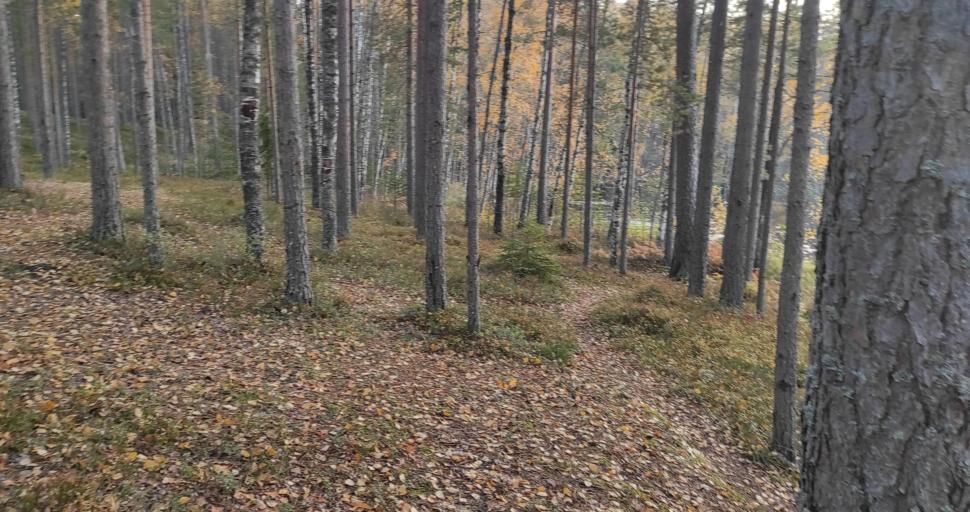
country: RU
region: Leningrad
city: Michurinskoye
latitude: 60.6236
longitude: 29.9243
